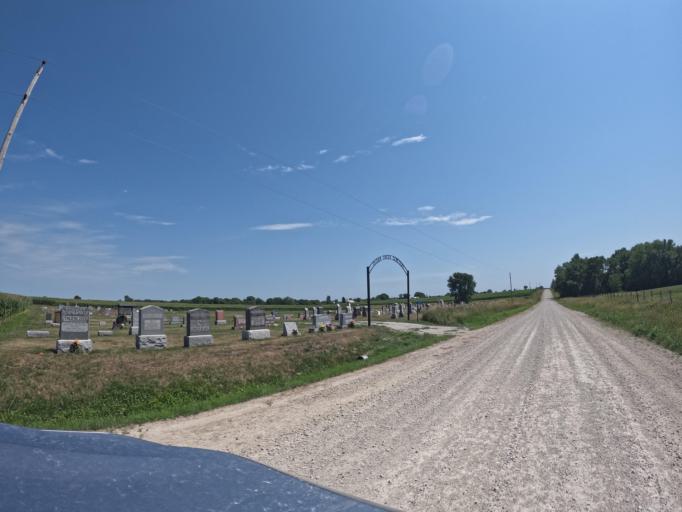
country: US
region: Iowa
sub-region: Henry County
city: Mount Pleasant
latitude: 40.9001
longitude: -91.6314
